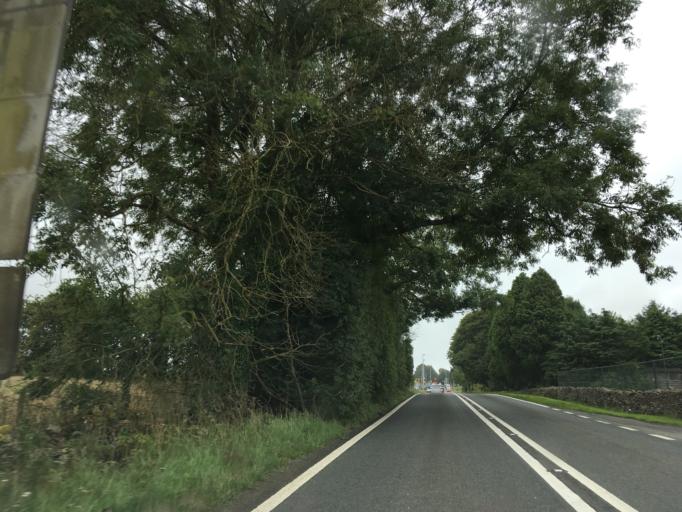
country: GB
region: England
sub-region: Somerset
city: Mendip
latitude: 51.2518
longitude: -2.6028
